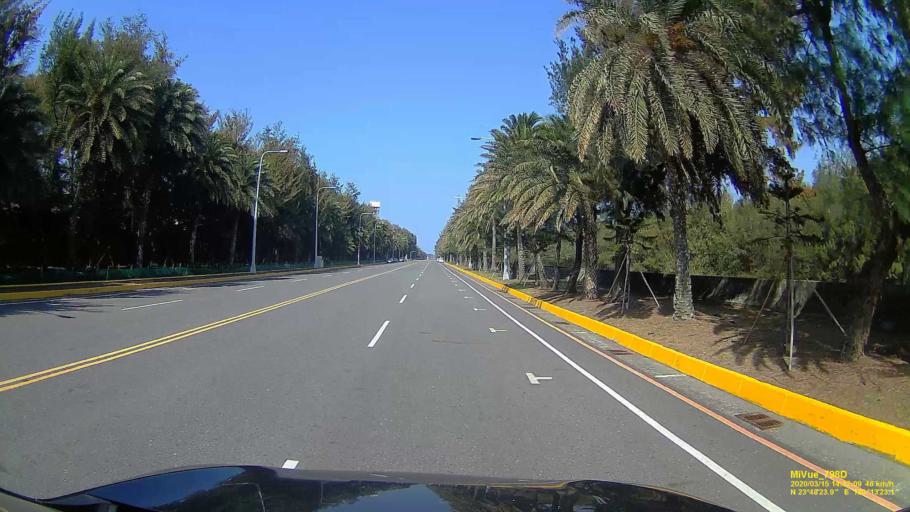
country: TW
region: Taiwan
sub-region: Yunlin
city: Douliu
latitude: 23.8069
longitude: 120.2233
